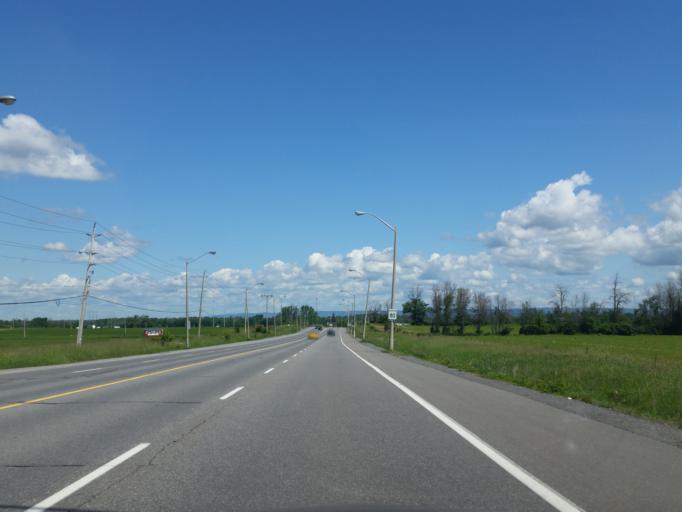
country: CA
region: Ontario
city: Bells Corners
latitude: 45.3305
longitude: -75.8379
